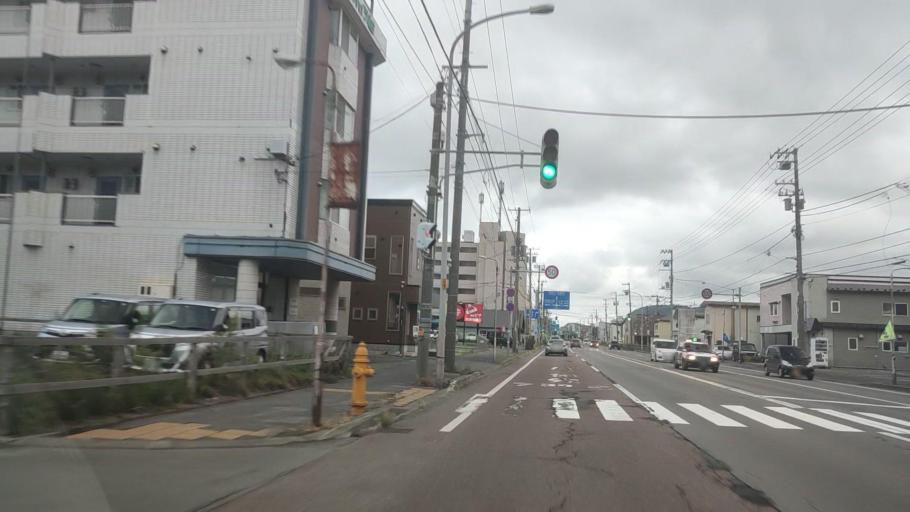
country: JP
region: Hokkaido
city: Hakodate
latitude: 41.7935
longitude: 140.7331
